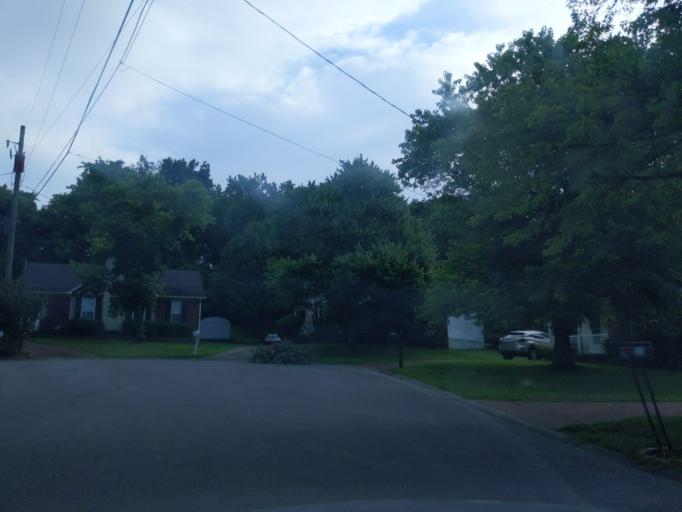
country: US
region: Tennessee
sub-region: Wilson County
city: Green Hill
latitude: 36.1853
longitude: -86.5992
